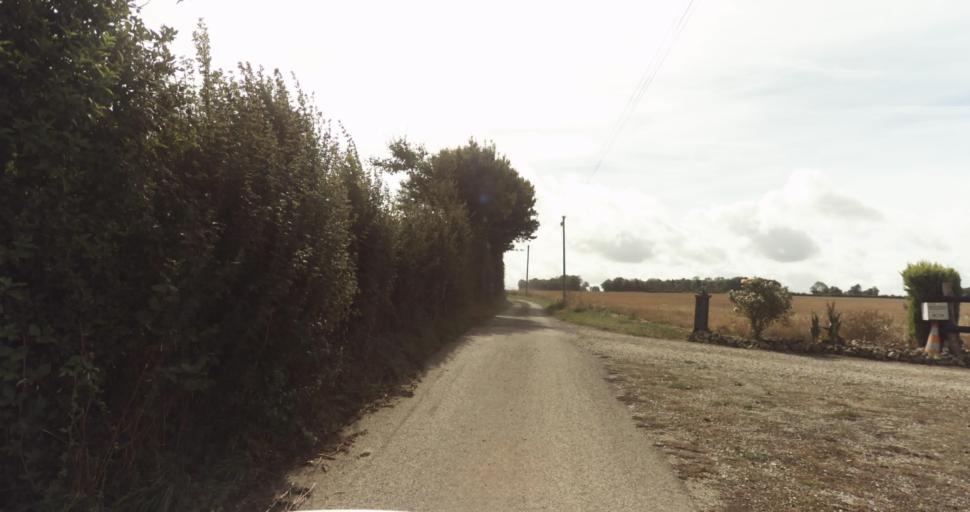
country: FR
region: Lower Normandy
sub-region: Departement de l'Orne
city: Gace
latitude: 48.8251
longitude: 0.3787
